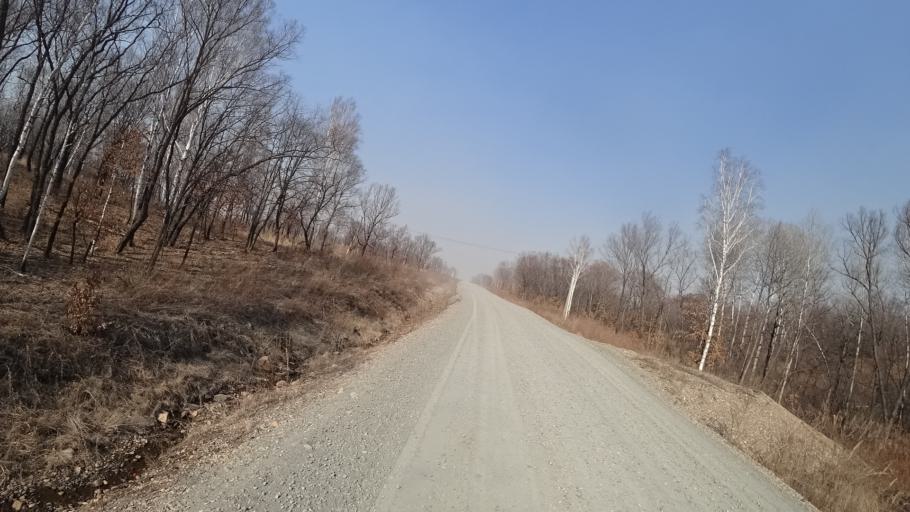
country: RU
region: Amur
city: Novobureyskiy
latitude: 49.8000
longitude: 129.9591
